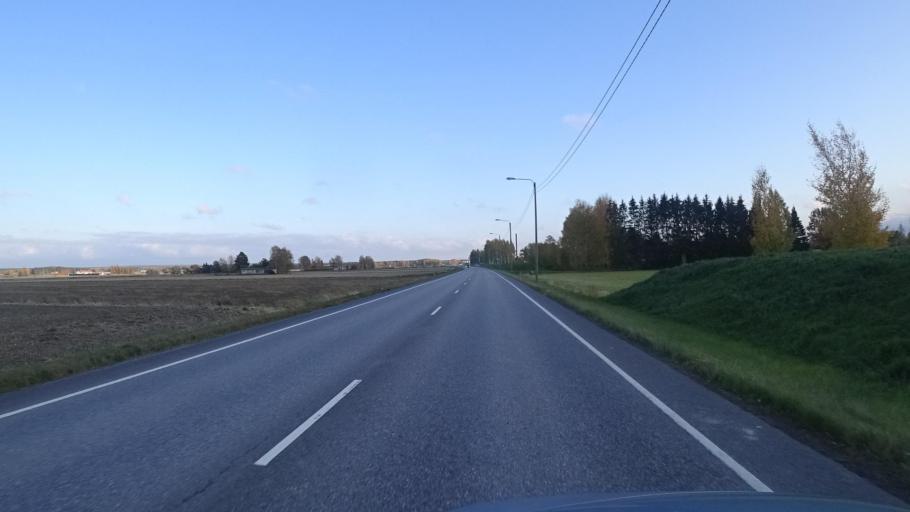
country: FI
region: Satakunta
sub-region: Rauma
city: Saekylae
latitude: 61.0517
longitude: 22.3422
